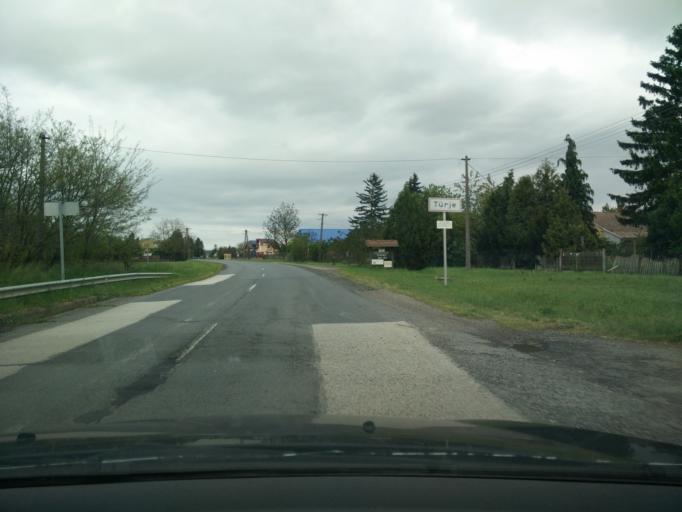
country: HU
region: Zala
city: Turje
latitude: 46.9868
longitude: 17.0739
